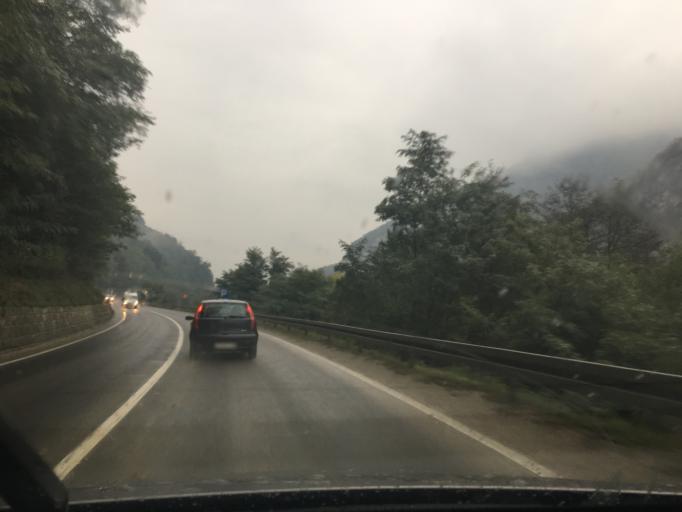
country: RS
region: Central Serbia
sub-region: Pcinjski Okrug
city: Vladicin Han
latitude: 42.7536
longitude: 22.0819
